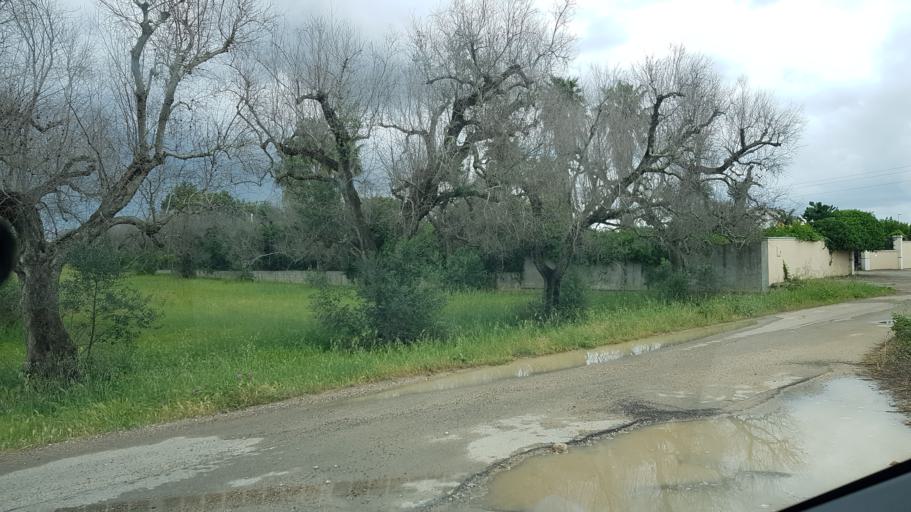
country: IT
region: Apulia
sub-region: Provincia di Brindisi
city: Torchiarolo
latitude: 40.4921
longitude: 18.0498
